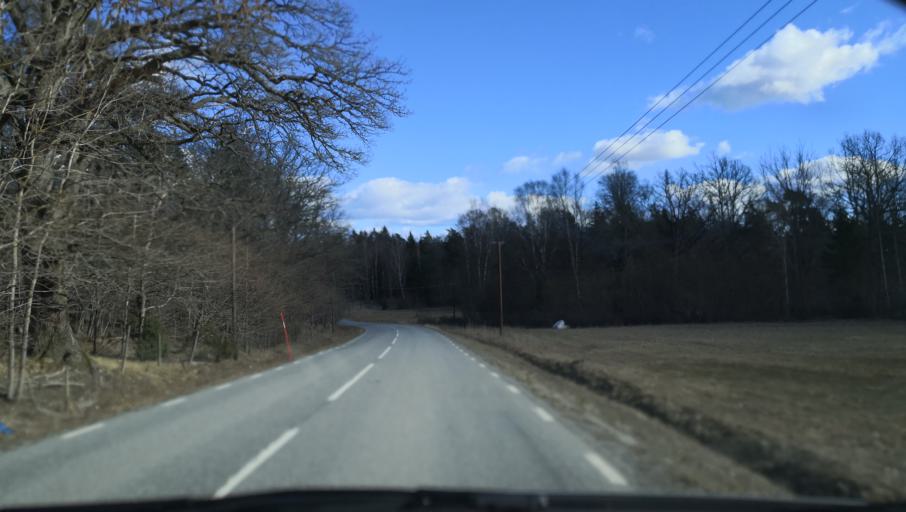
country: SE
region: Stockholm
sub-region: Varmdo Kommun
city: Hemmesta
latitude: 59.3601
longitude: 18.5407
